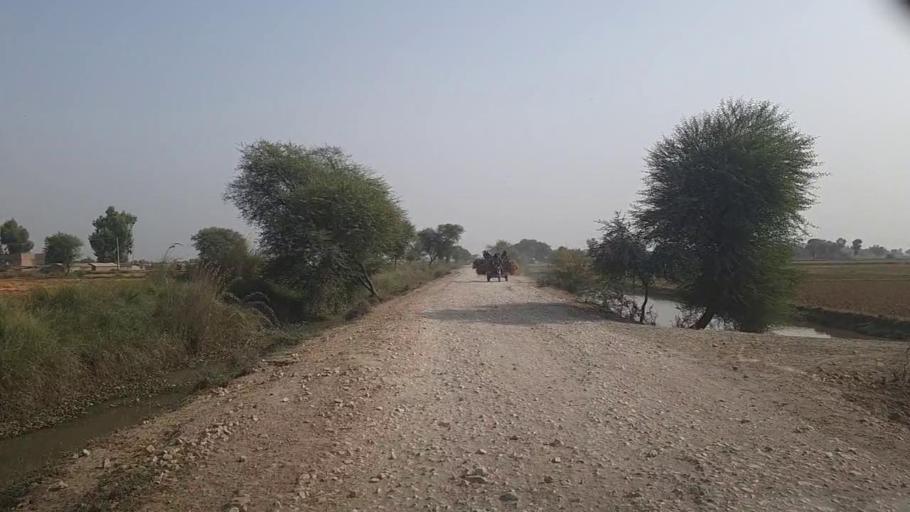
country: PK
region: Sindh
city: Kashmor
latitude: 28.3669
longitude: 69.5526
